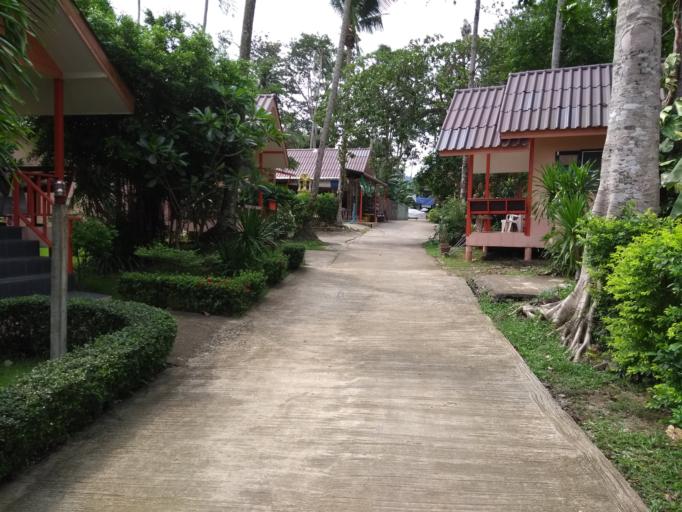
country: TH
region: Trat
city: Ko Chang Tai
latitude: 12.0018
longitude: 102.2947
